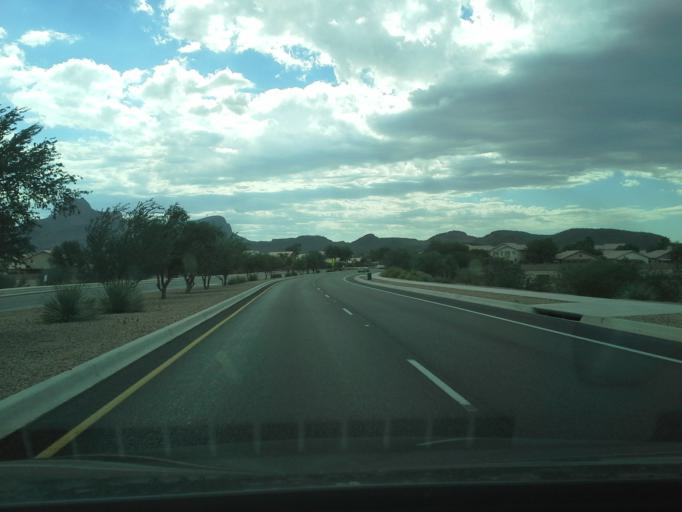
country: US
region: Arizona
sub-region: Pima County
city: Tortolita
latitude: 32.3754
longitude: -111.1167
